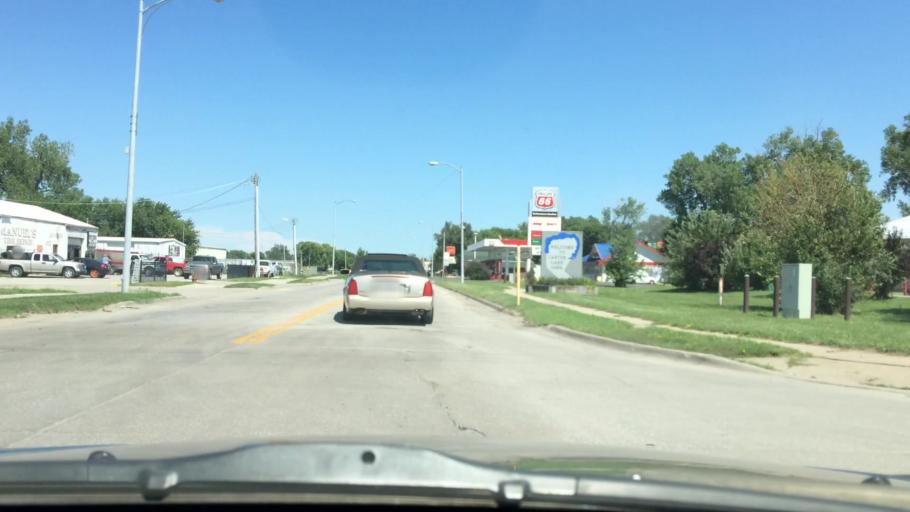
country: US
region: Iowa
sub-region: Pottawattamie County
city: Carter Lake
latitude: 41.2851
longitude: -95.9302
